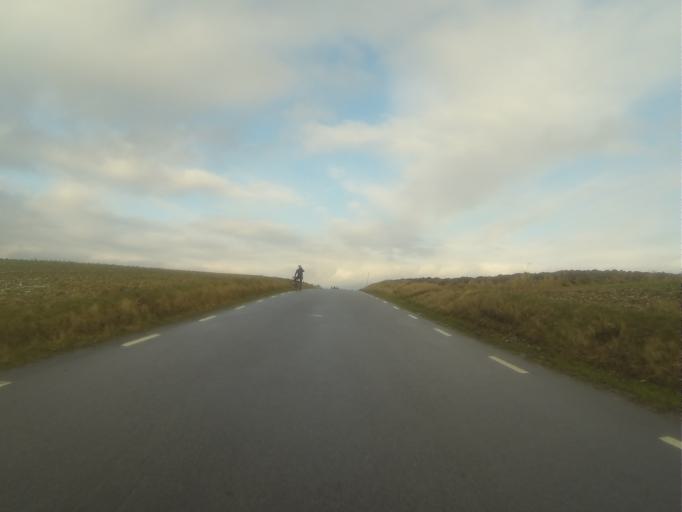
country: SE
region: Skane
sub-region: Svedala Kommun
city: Klagerup
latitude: 55.6153
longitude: 13.3077
